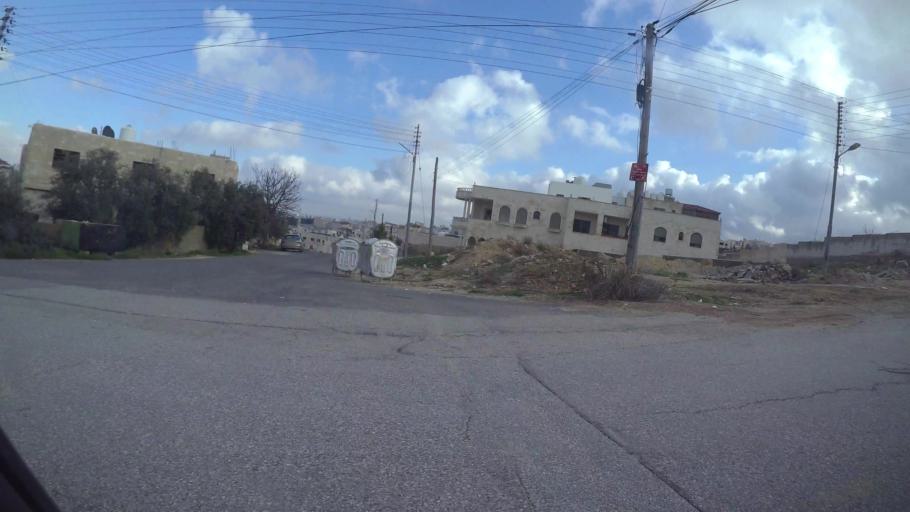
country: JO
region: Amman
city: Al Jubayhah
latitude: 32.0542
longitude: 35.8977
